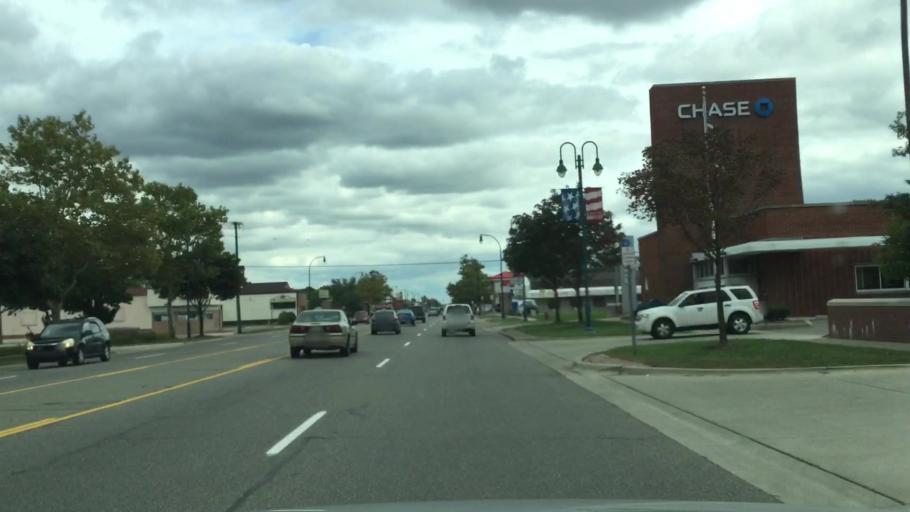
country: US
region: Michigan
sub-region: Wayne County
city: Garden City
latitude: 42.3256
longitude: -83.3270
